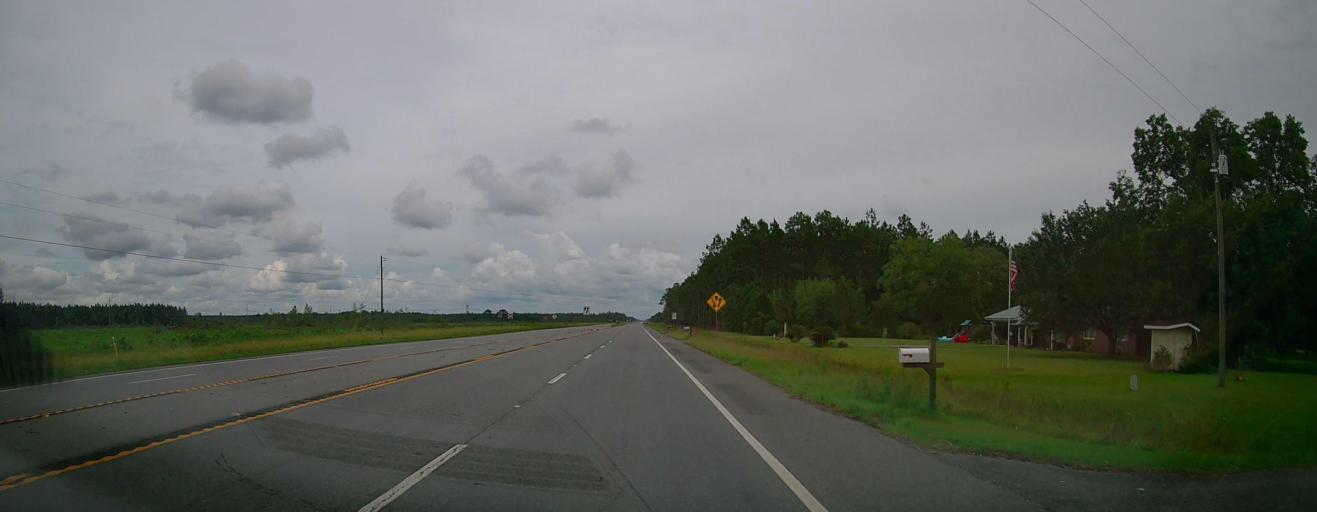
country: US
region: Georgia
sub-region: Appling County
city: Baxley
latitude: 31.7605
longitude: -82.2970
